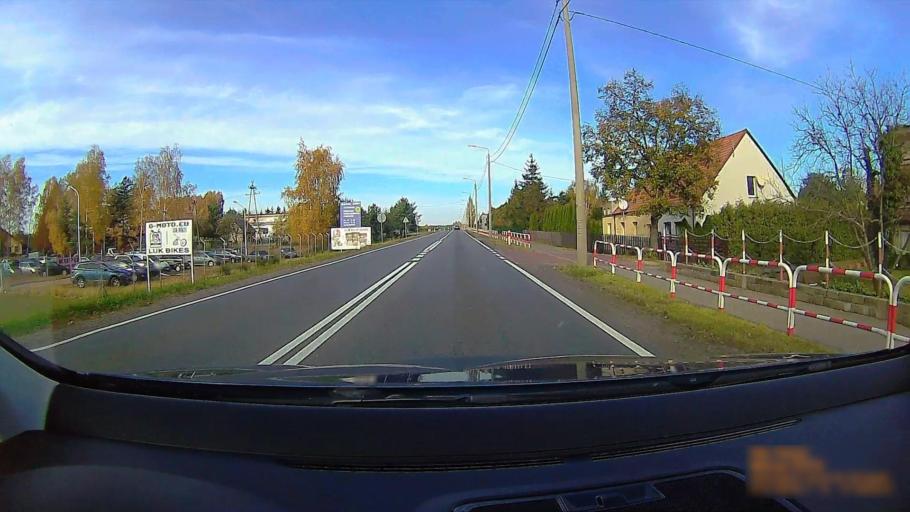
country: PL
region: Greater Poland Voivodeship
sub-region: Powiat ostrzeszowski
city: Ostrzeszow
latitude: 51.4377
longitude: 17.9148
